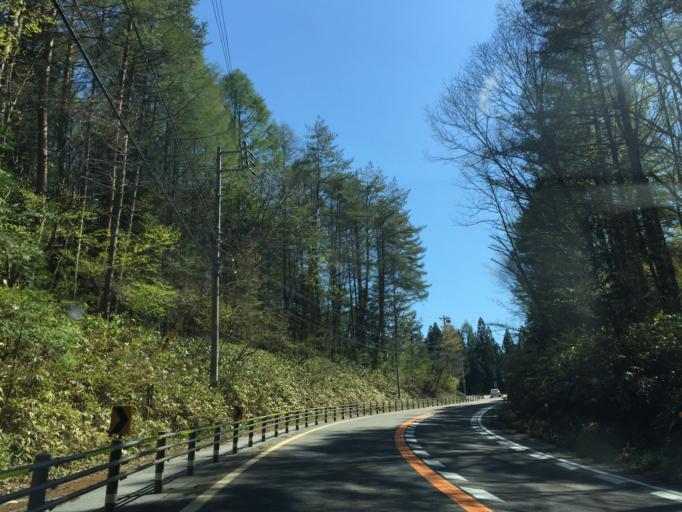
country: JP
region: Gifu
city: Nakatsugawa
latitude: 35.3602
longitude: 137.6727
